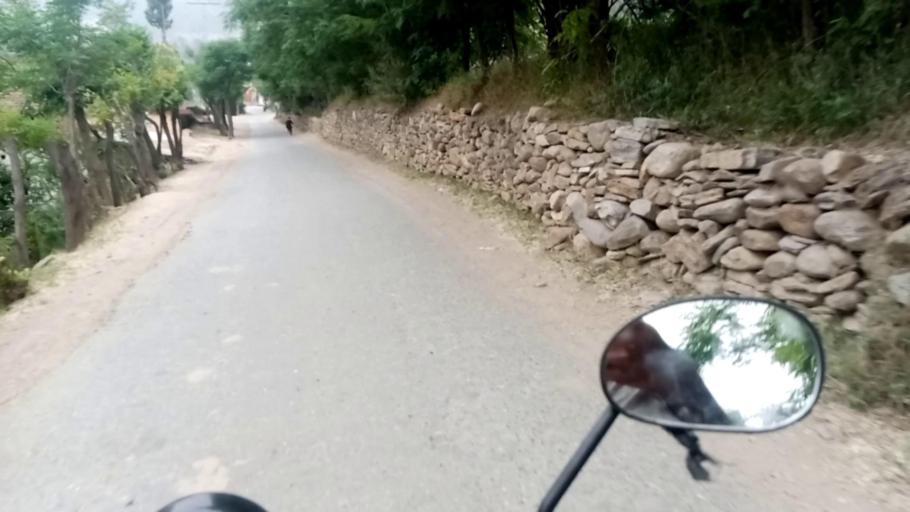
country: PK
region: Khyber Pakhtunkhwa
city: Saidu Sharif
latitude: 34.7549
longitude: 72.3785
